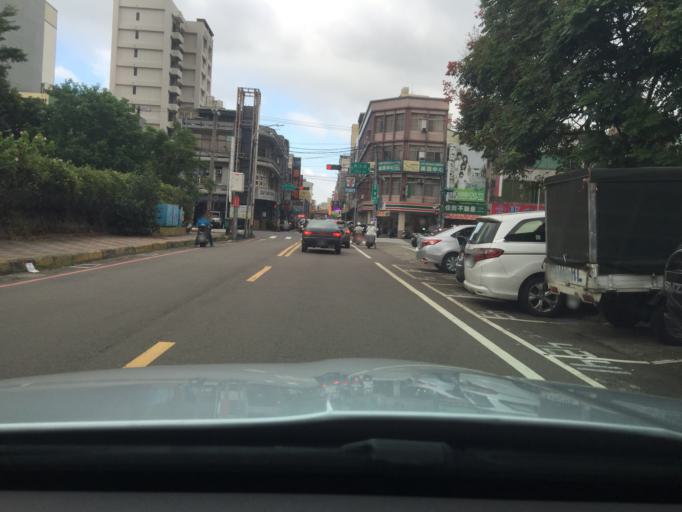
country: TW
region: Taiwan
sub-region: Hsinchu
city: Hsinchu
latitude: 24.8075
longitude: 120.9606
